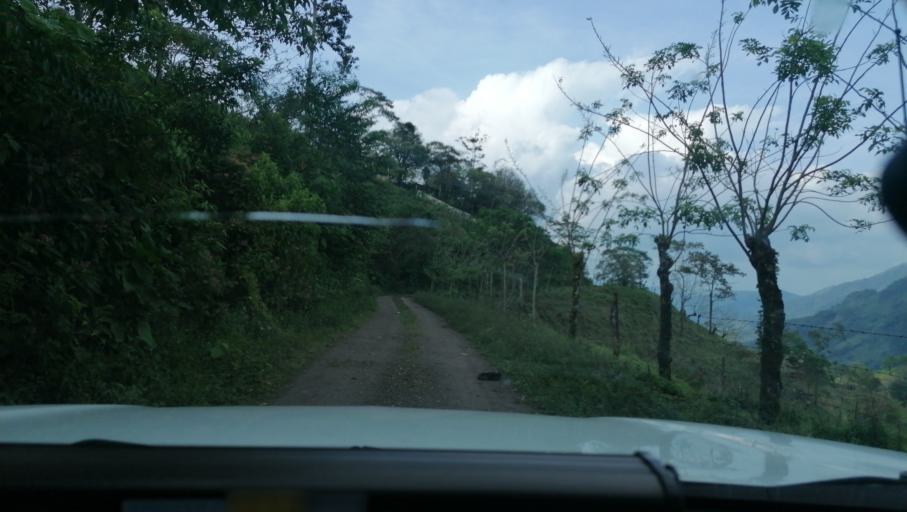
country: MX
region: Chiapas
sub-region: Tapilula
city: San Francisco Jacona
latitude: 17.3132
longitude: -93.1014
